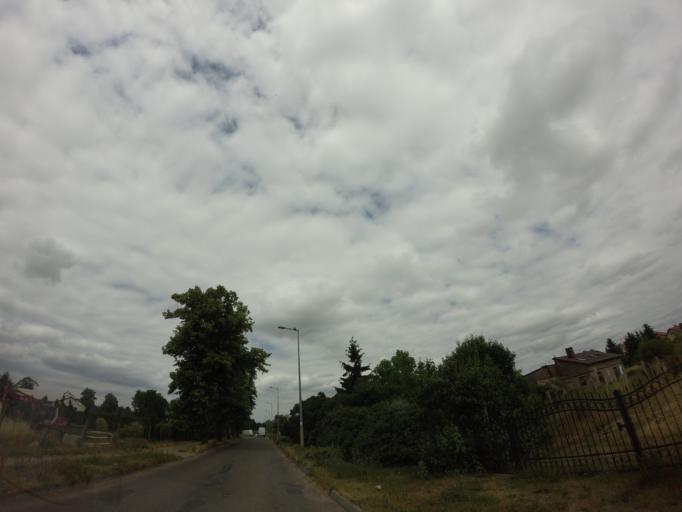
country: PL
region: Lubusz
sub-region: Powiat strzelecko-drezdenecki
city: Strzelce Krajenskie
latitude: 52.8793
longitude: 15.5448
